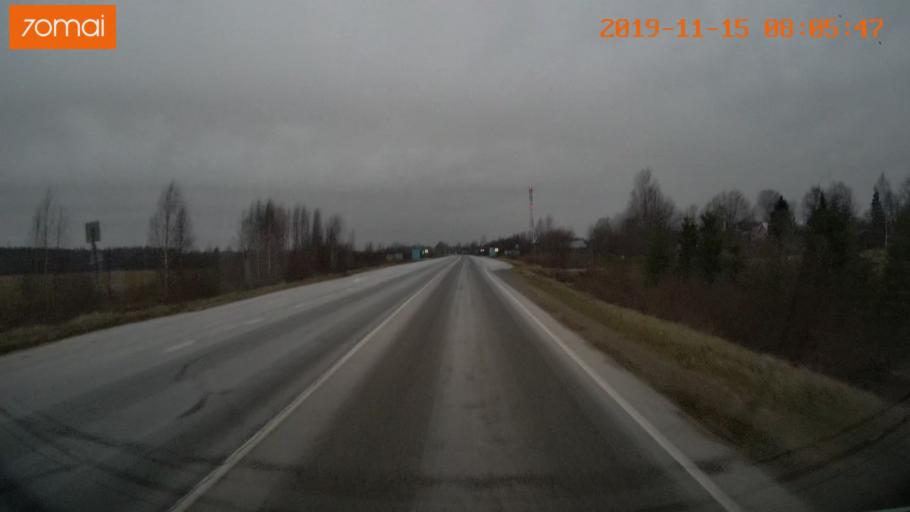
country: RU
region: Vologda
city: Cherepovets
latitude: 59.0182
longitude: 38.0521
